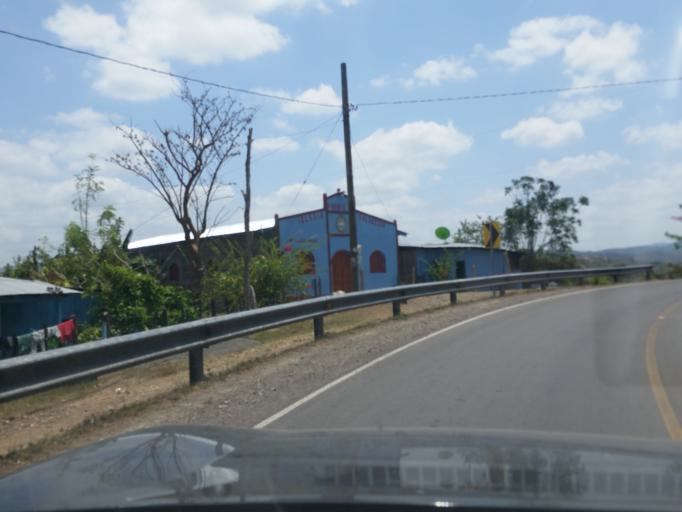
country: NI
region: Matagalpa
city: Muy Muy
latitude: 12.6156
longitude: -85.5345
